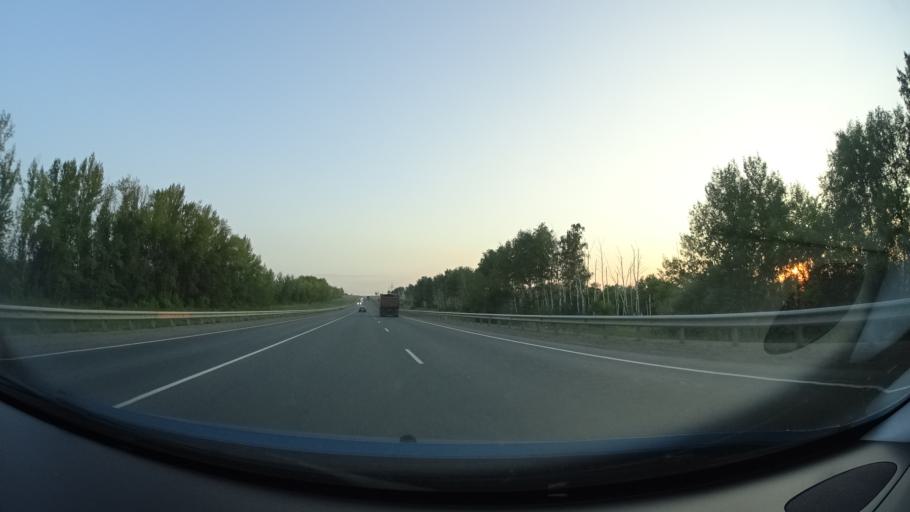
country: RU
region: Samara
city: Sukhodol
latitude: 53.8688
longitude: 51.1970
